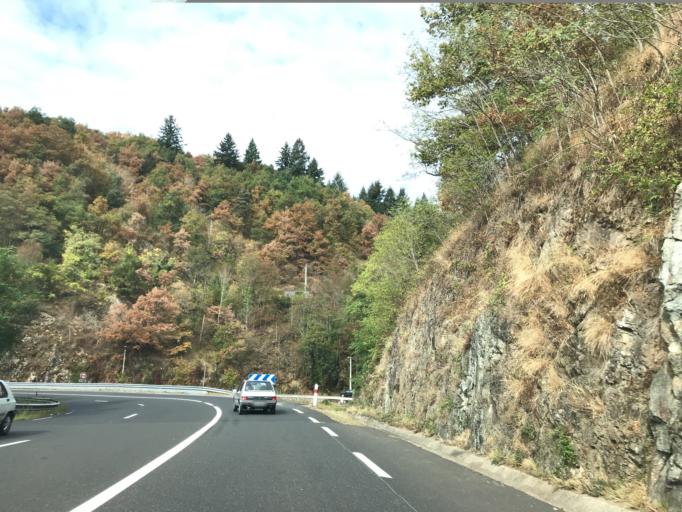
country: FR
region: Auvergne
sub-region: Departement du Puy-de-Dome
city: Thiers
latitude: 45.8653
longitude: 3.5632
